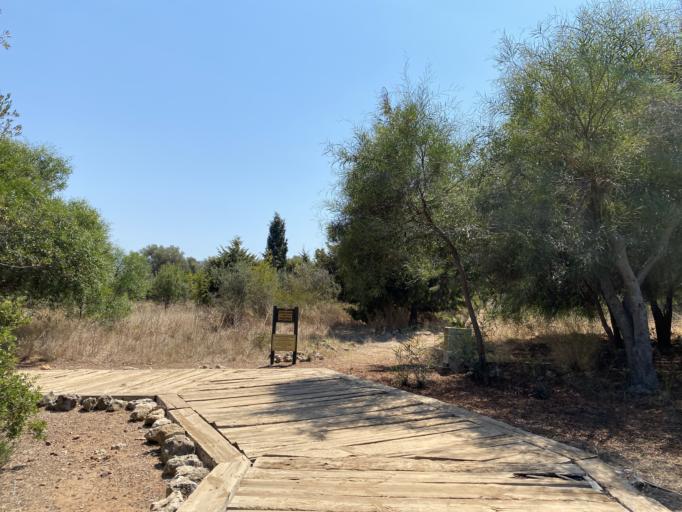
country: TR
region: Mugla
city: Yerkesik
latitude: 36.9922
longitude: 28.2036
